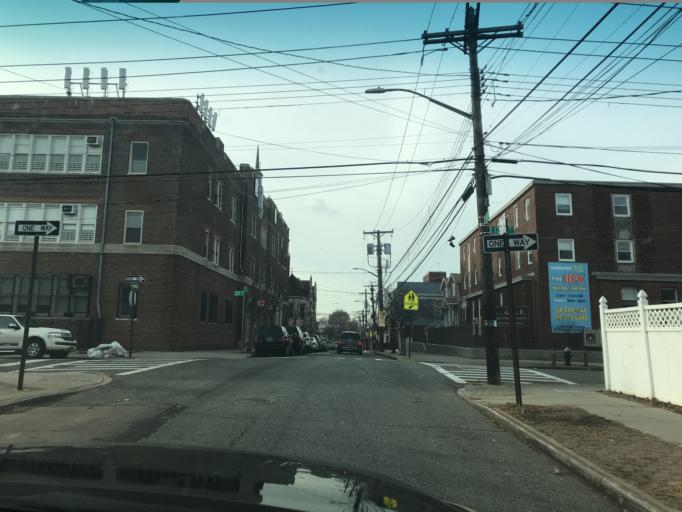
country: US
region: New York
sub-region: Bronx
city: The Bronx
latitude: 40.7853
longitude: -73.8426
